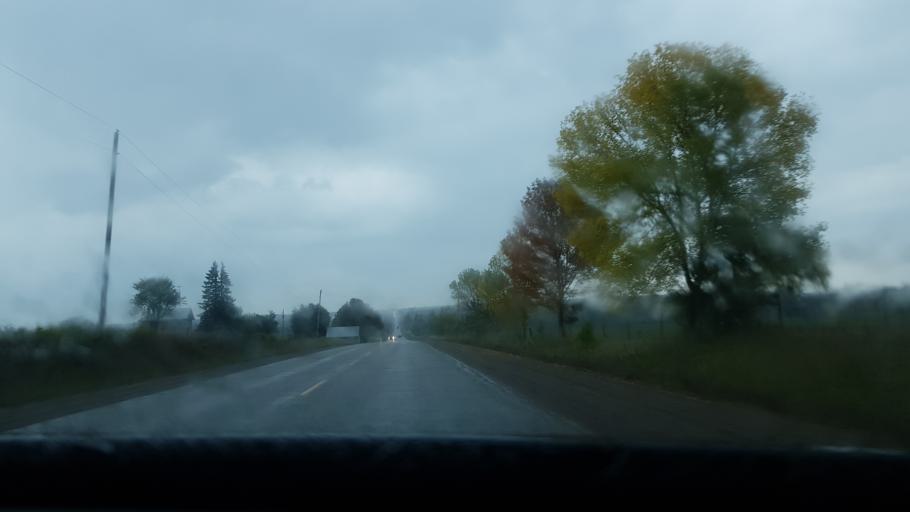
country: CA
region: Ontario
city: Omemee
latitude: 44.3891
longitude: -78.5793
